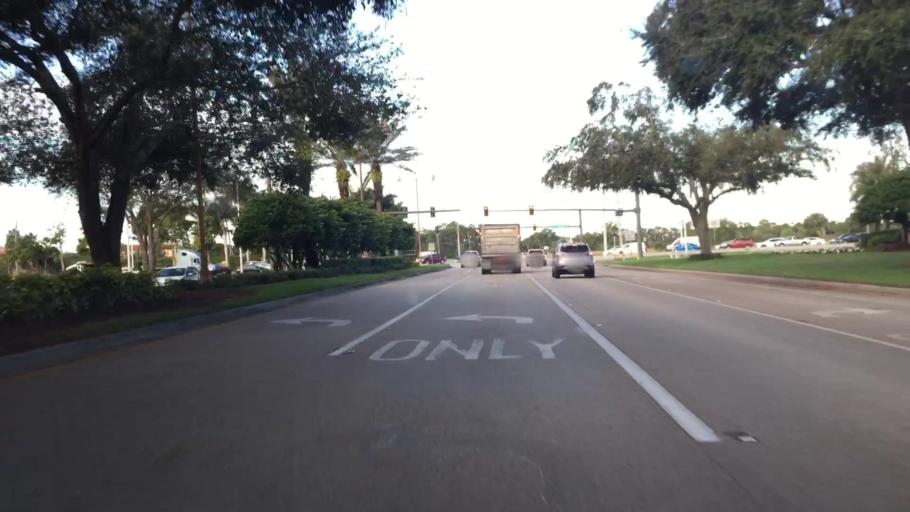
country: US
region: Florida
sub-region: Lee County
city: Estero
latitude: 26.3981
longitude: -81.8094
